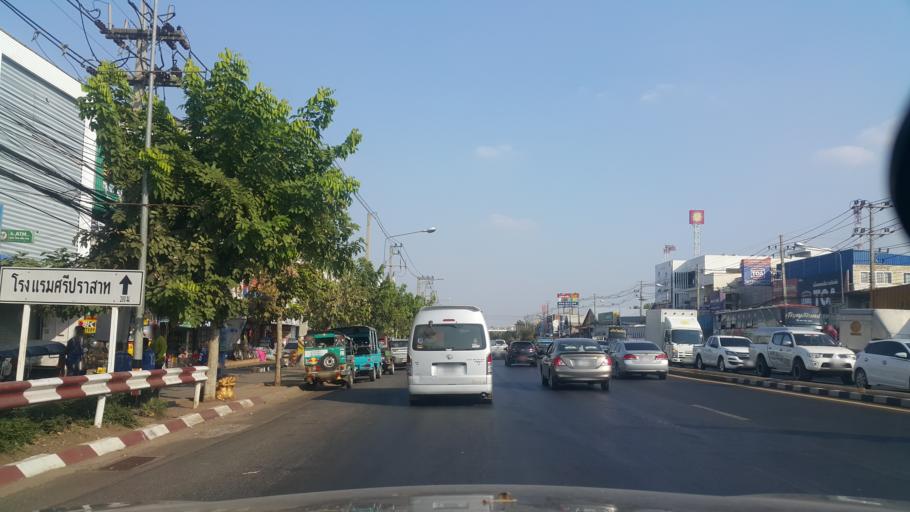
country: TH
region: Buriram
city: Nong Ki
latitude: 14.6844
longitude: 102.5393
